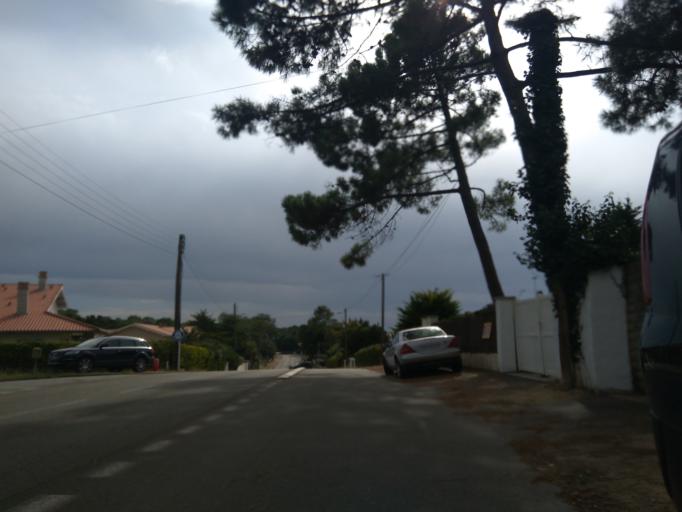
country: FR
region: Aquitaine
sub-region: Departement des Landes
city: Capbreton
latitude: 43.6443
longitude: -1.4410
